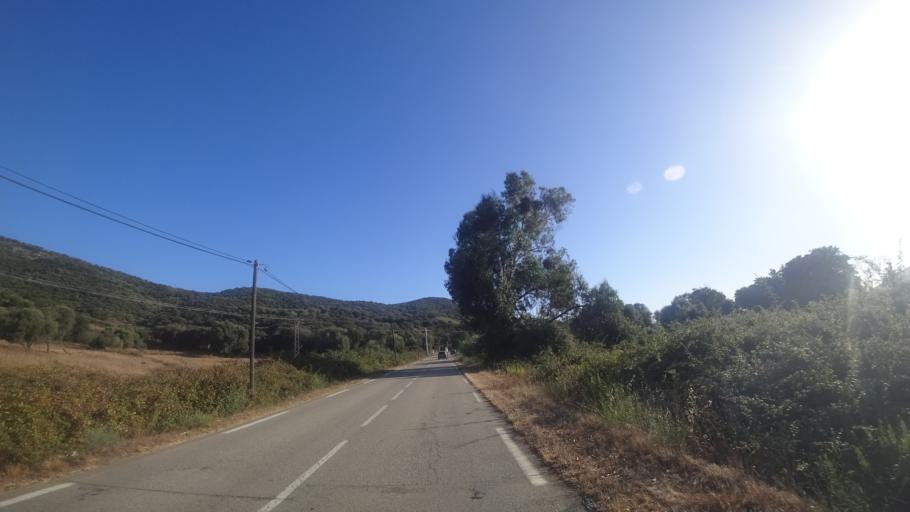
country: FR
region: Corsica
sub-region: Departement de la Corse-du-Sud
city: Cargese
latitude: 42.1746
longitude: 8.6115
